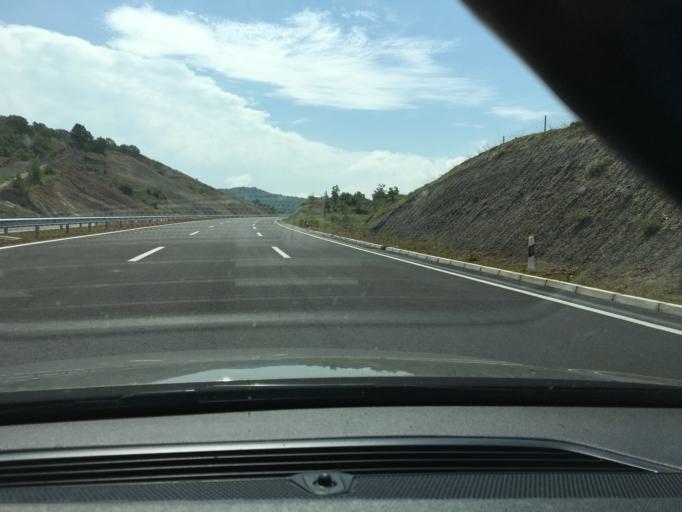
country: MK
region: Petrovec
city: Sredno Konjare
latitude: 41.9474
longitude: 21.7782
